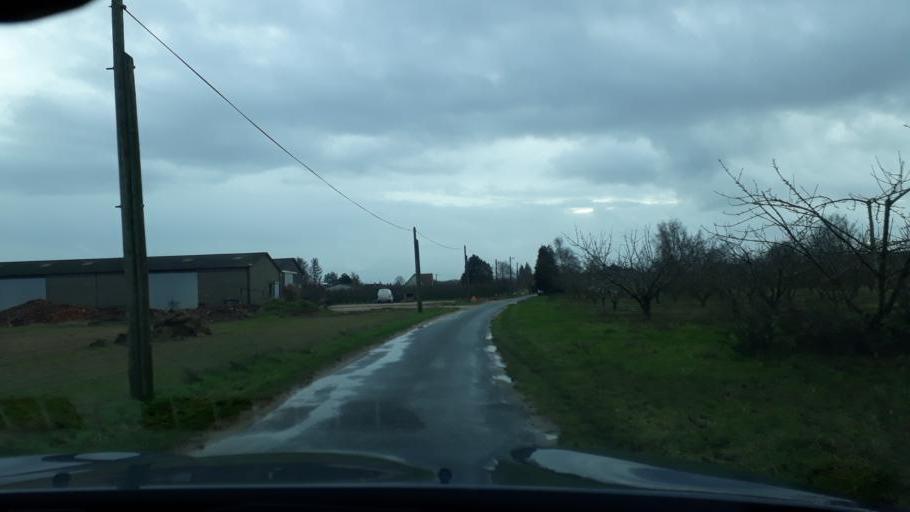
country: FR
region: Centre
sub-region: Departement du Loiret
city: Mareau-aux-Pres
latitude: 47.8318
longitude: 1.8012
